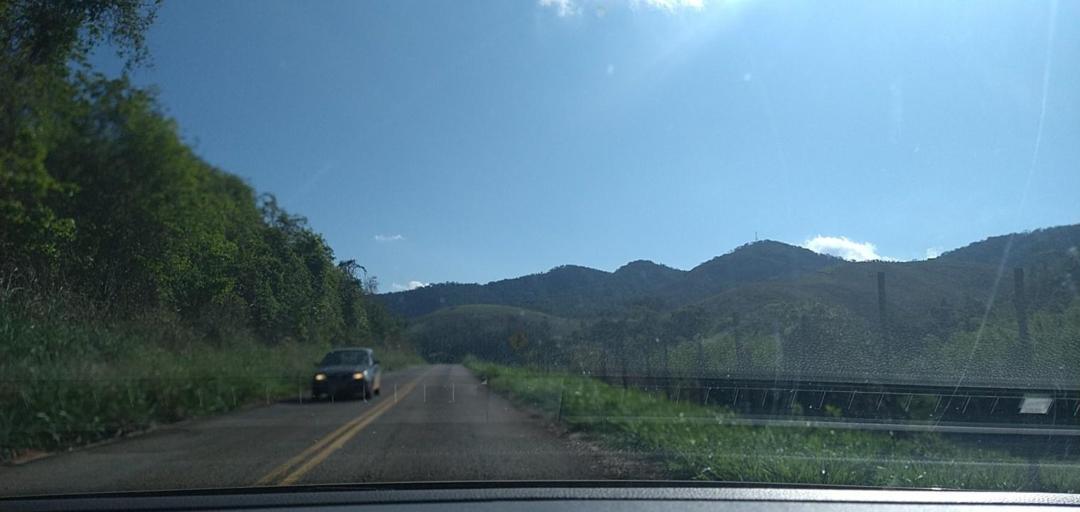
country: BR
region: Minas Gerais
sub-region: Alvinopolis
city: Alvinopolis
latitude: -20.1843
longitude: -42.9342
